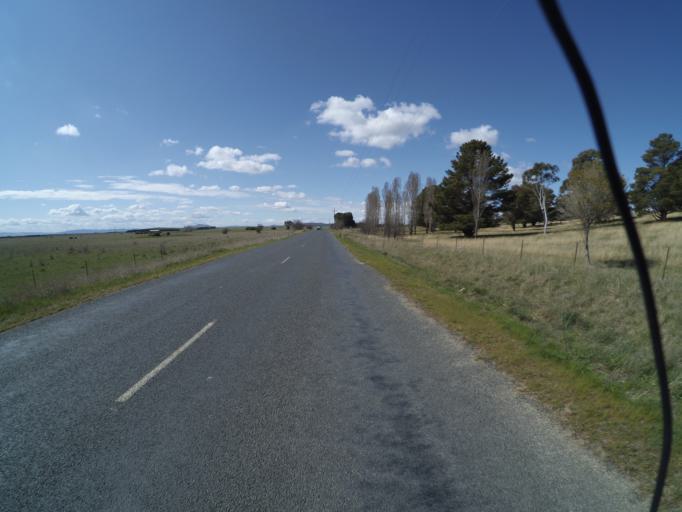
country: AU
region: New South Wales
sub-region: Palerang
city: Bungendore
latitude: -35.2300
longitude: 149.4485
